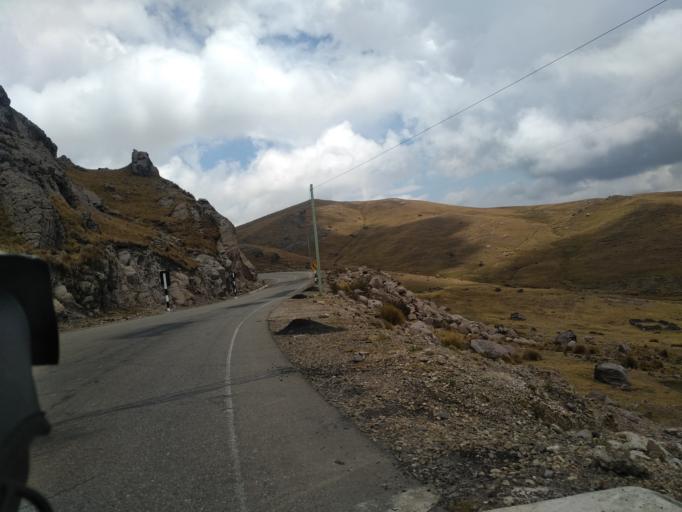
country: PE
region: La Libertad
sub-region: Provincia de Santiago de Chuco
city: Quiruvilca
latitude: -7.9738
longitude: -78.2163
